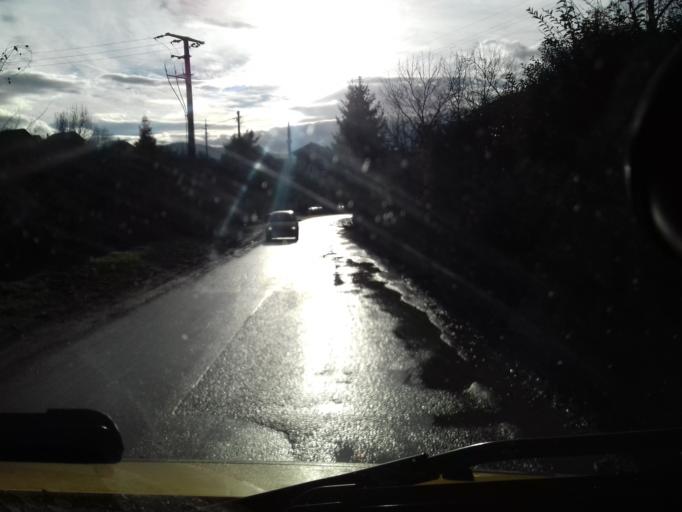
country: BA
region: Federation of Bosnia and Herzegovina
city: Zenica
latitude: 44.2112
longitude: 17.9324
